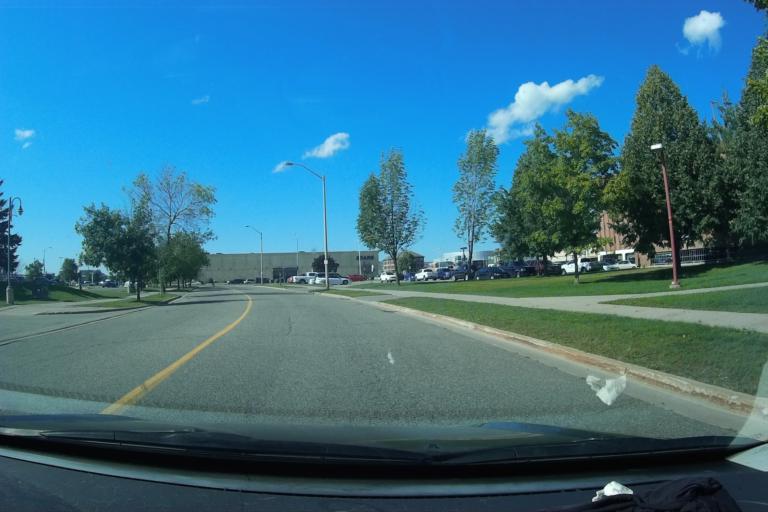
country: CA
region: Ontario
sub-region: Algoma
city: Sault Ste. Marie
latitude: 46.5096
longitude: -84.3356
